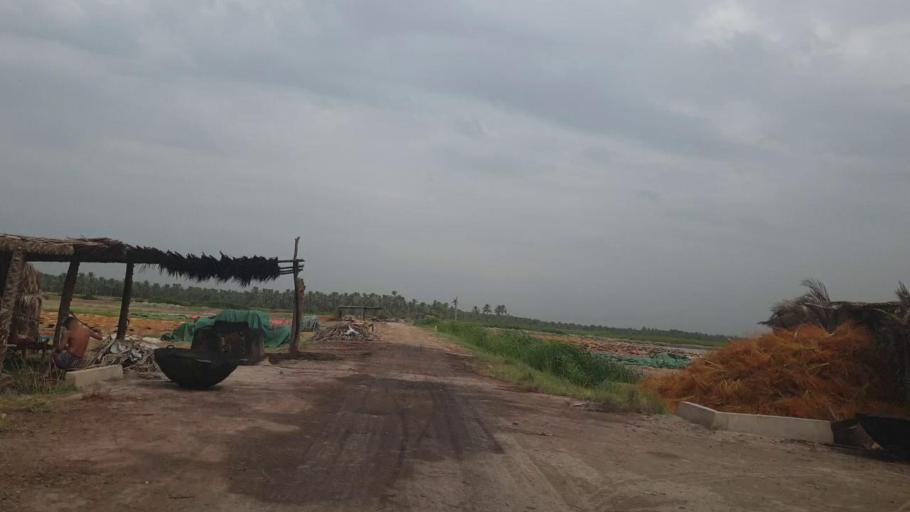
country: PK
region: Sindh
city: Khairpur
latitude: 27.5842
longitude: 68.7398
